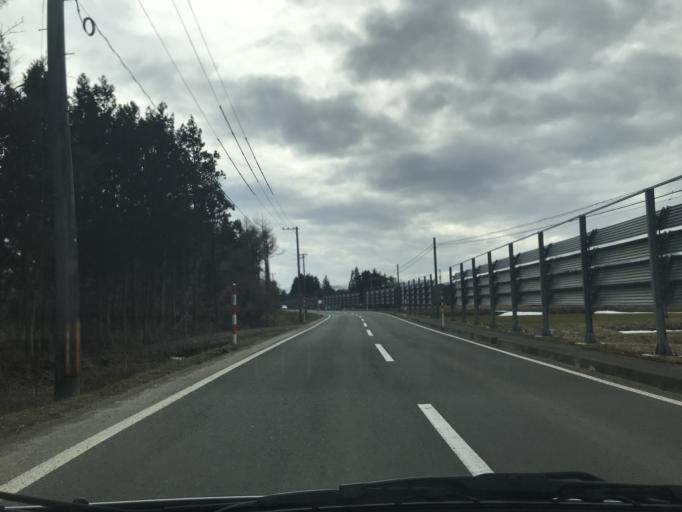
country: JP
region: Iwate
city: Hanamaki
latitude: 39.3765
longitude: 141.0067
